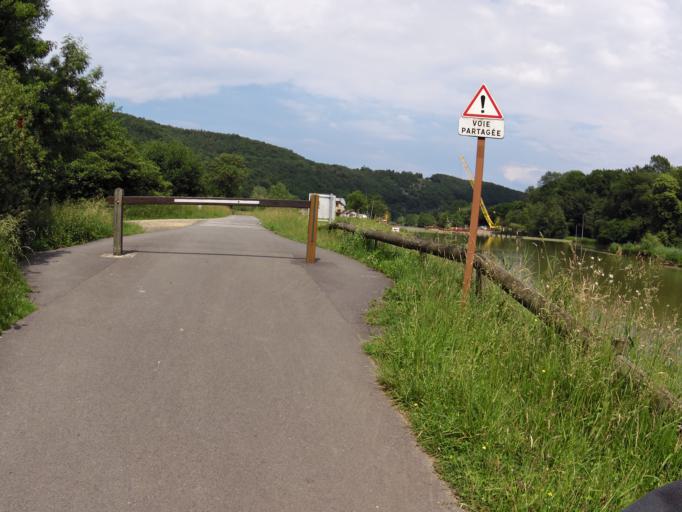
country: FR
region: Champagne-Ardenne
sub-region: Departement des Ardennes
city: Nouzonville
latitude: 49.8341
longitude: 4.7510
